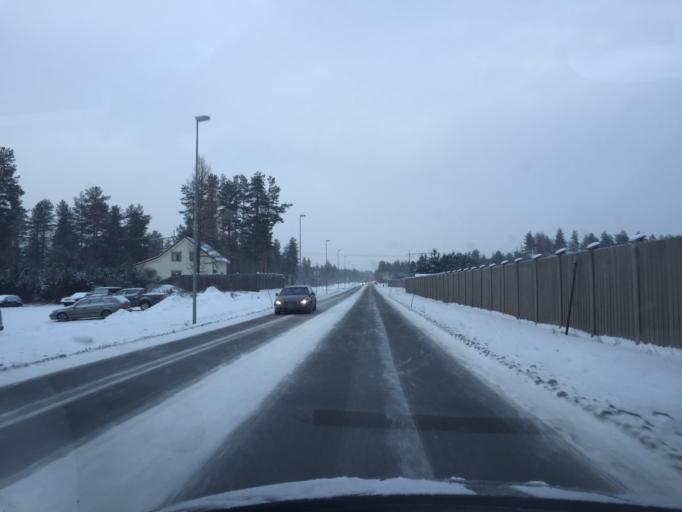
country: NO
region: Hedmark
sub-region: Elverum
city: Elverum
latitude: 60.9001
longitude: 11.5946
